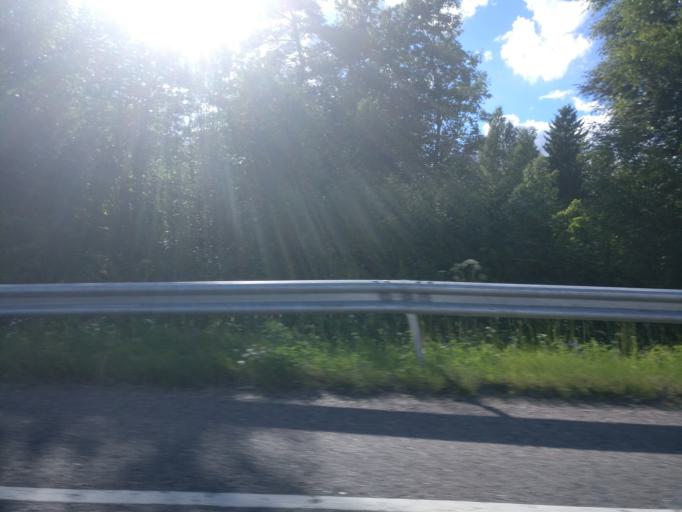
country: FI
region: Uusimaa
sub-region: Helsinki
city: Vihti
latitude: 60.4302
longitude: 24.4726
